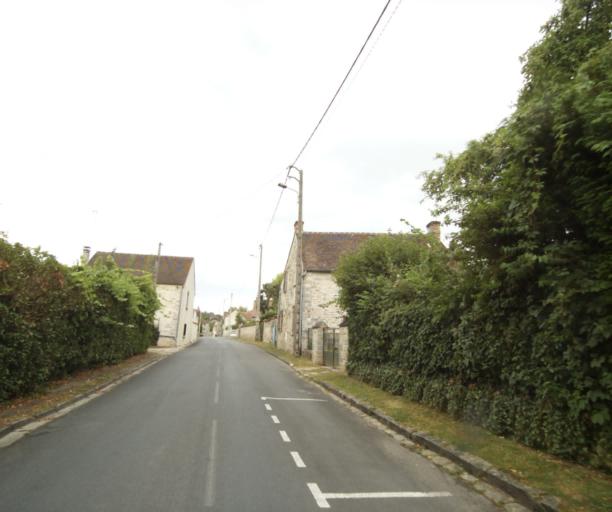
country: FR
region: Ile-de-France
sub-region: Departement de Seine-et-Marne
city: Cely
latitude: 48.4614
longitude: 2.5243
